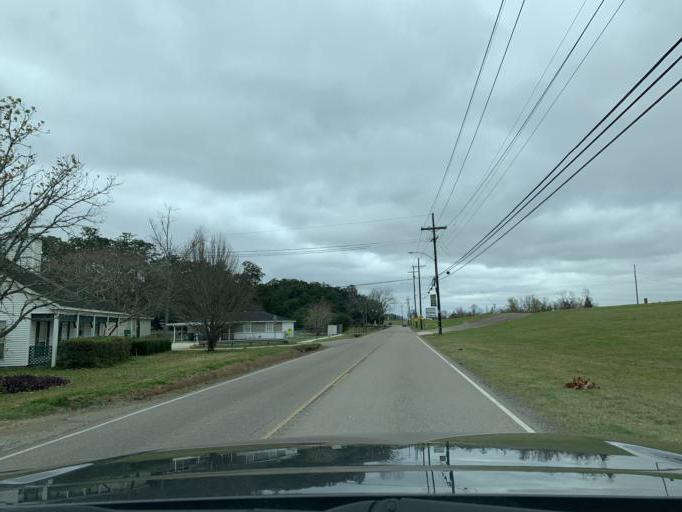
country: US
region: Louisiana
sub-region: Jefferson Parish
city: River Ridge
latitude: 29.9536
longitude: -90.2339
